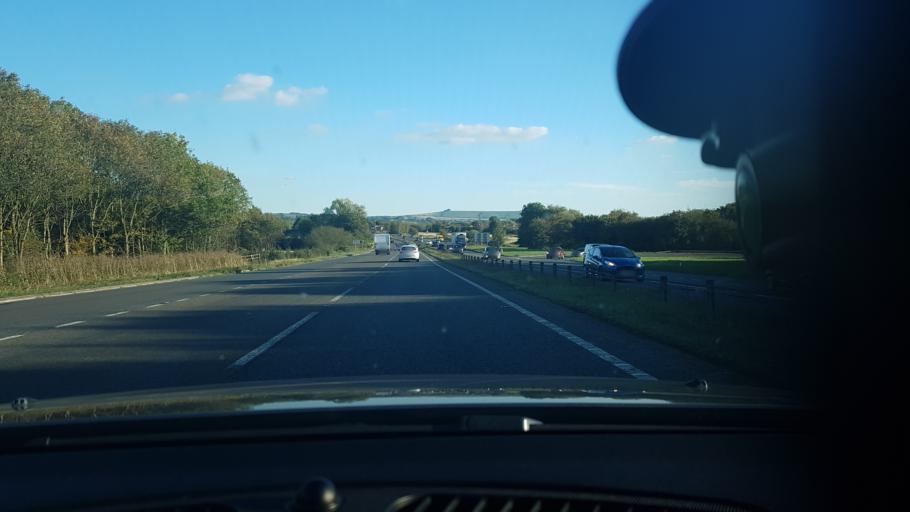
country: GB
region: England
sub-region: Borough of Swindon
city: Wanborough
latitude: 51.5737
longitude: -1.7311
